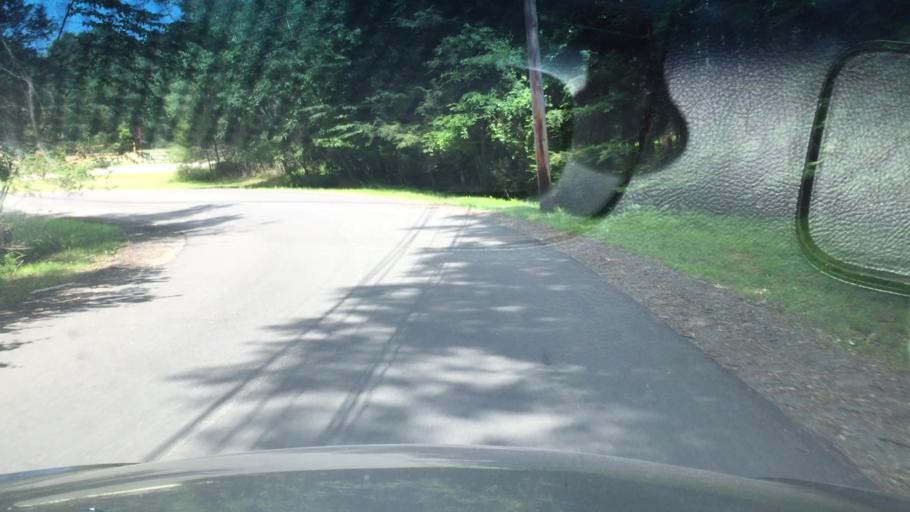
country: US
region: Pennsylvania
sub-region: Luzerne County
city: Freeland
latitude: 41.0490
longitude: -75.9157
